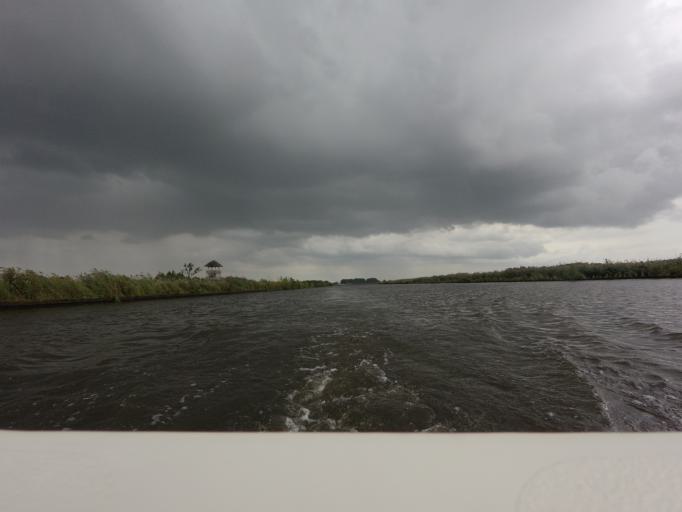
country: NL
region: Friesland
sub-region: Gemeente Smallingerland
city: Oudega
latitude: 53.1157
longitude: 5.9463
